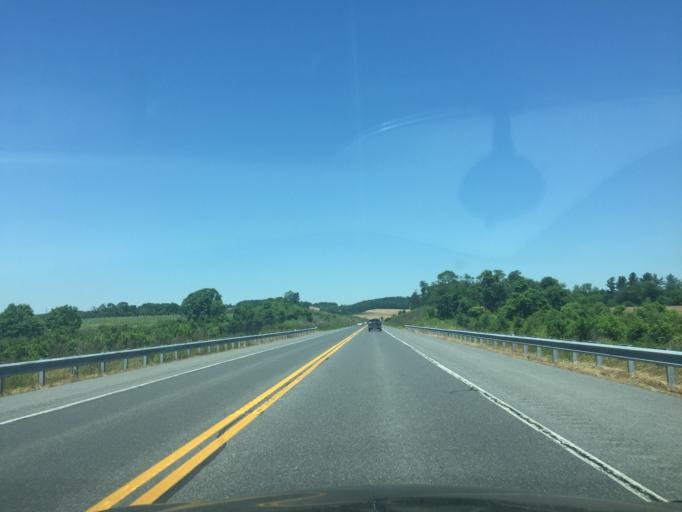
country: US
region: Maryland
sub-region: Carroll County
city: Hampstead
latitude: 39.6207
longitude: -76.8635
